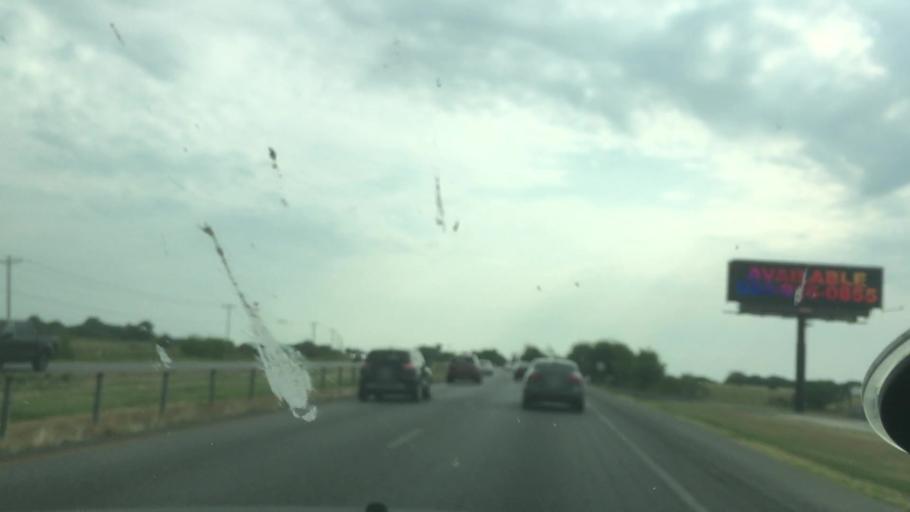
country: US
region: Oklahoma
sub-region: Bryan County
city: Colbert
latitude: 33.8971
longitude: -96.4733
